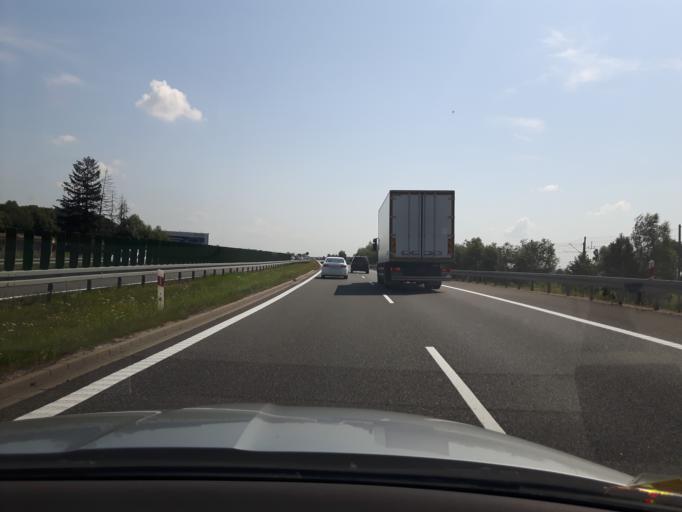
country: PL
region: Warmian-Masurian Voivodeship
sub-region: Powiat elblaski
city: Gronowo Gorne
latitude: 54.1096
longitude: 19.4892
